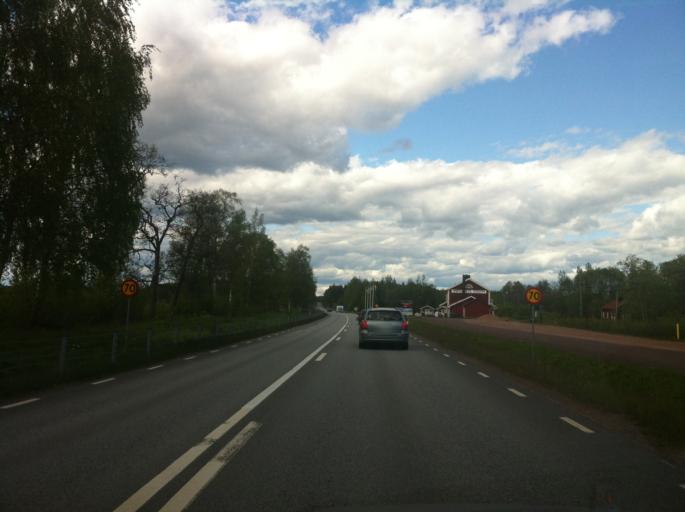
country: SE
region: Vaermland
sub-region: Storfors Kommun
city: Storfors
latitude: 59.4329
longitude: 14.2286
